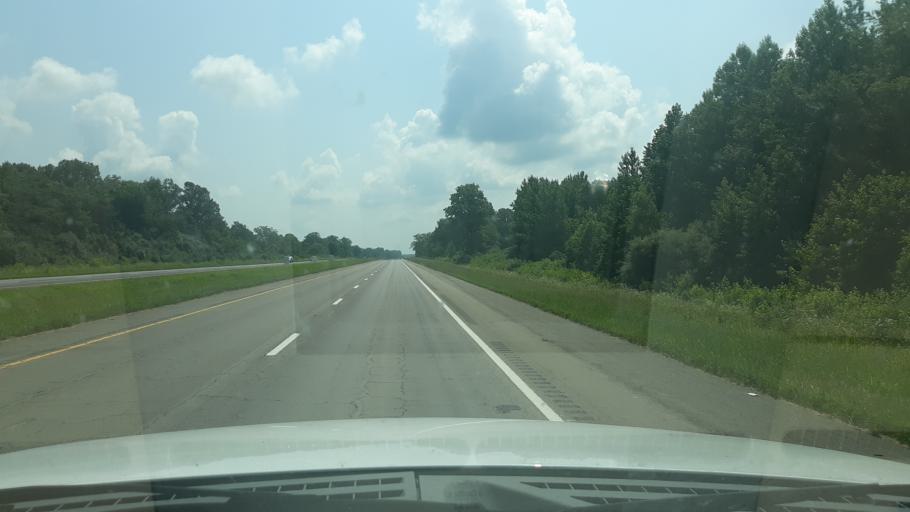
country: US
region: Illinois
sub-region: Saline County
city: Carrier Mills
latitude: 37.7334
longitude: -88.6597
